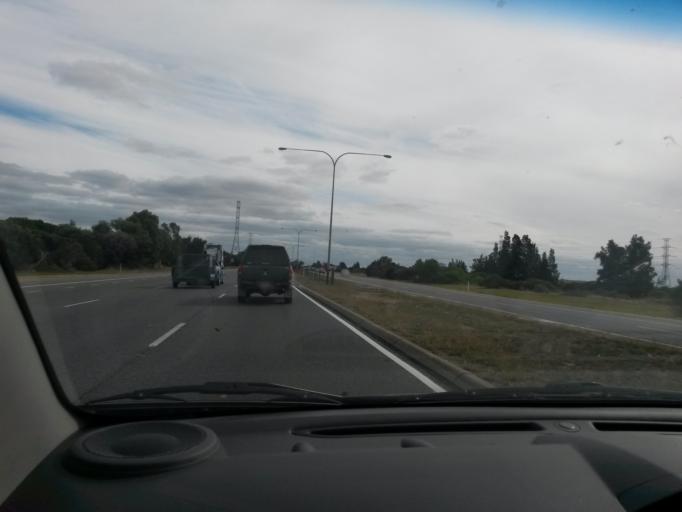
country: AU
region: South Australia
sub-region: Port Adelaide Enfield
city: Enfield
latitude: -34.8152
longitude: 138.5943
